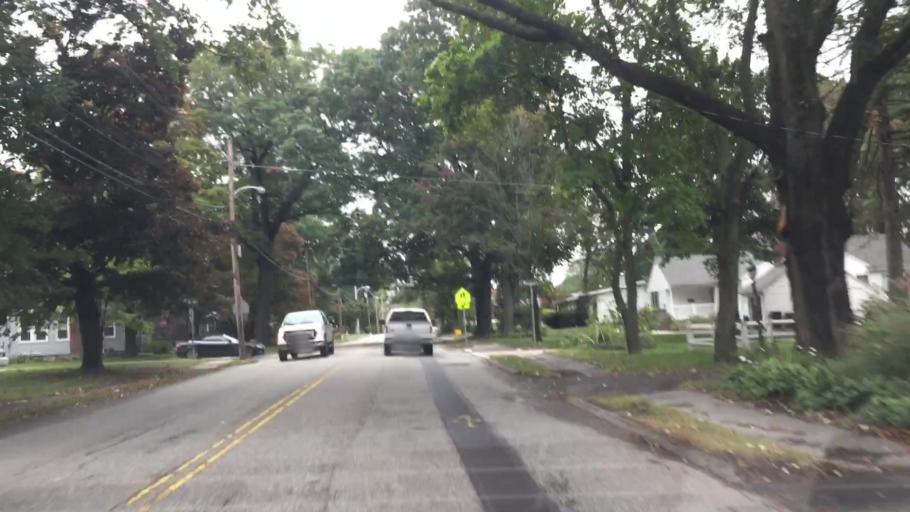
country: US
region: Massachusetts
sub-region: Essex County
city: North Andover
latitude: 42.6909
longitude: -71.1283
